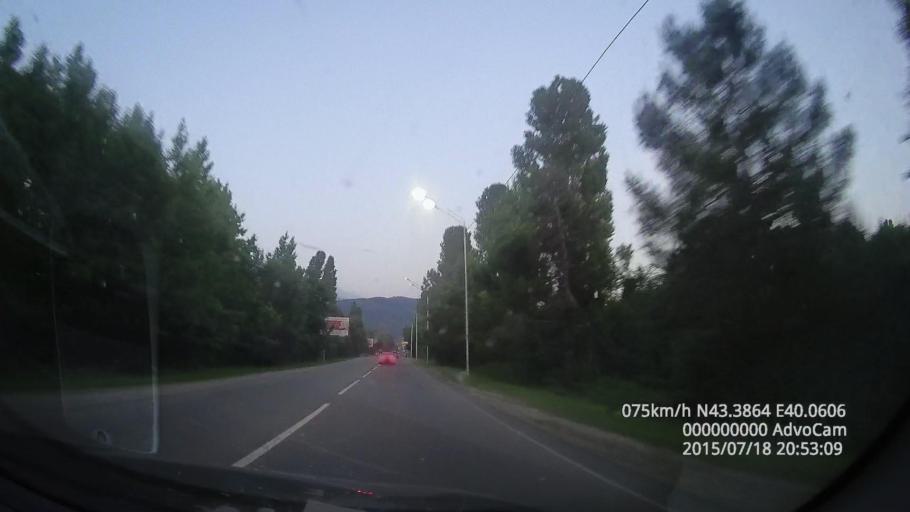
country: GE
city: Gantiadi
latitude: 43.3862
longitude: 40.0624
